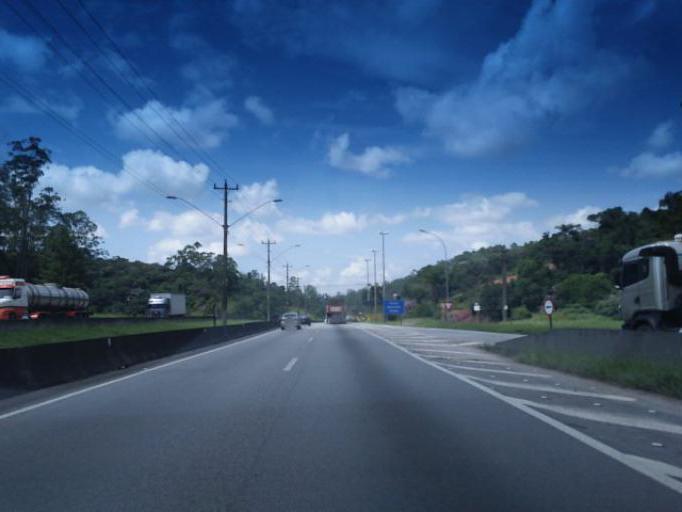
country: BR
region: Sao Paulo
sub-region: Itapecerica Da Serra
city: Itapecerica da Serra
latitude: -23.7687
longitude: -46.9100
